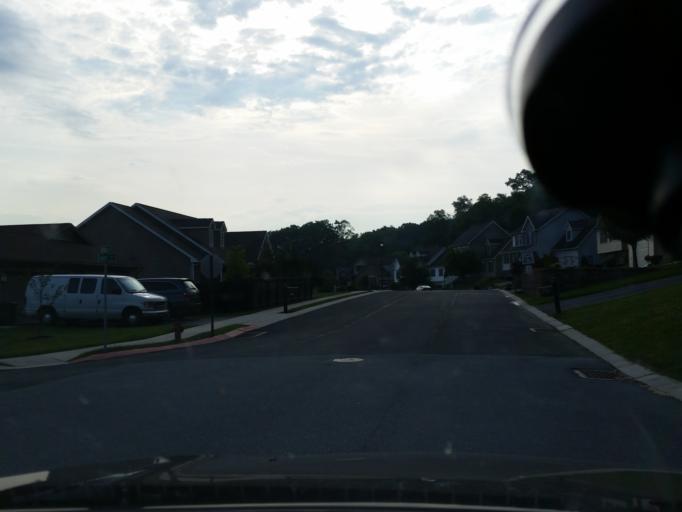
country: US
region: Pennsylvania
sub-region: Perry County
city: Marysville
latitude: 40.3328
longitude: -76.9385
